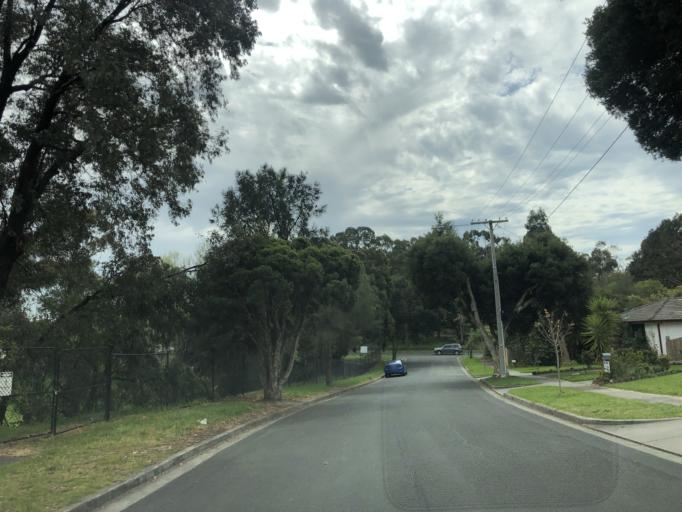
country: AU
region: Victoria
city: Burwood East
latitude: -37.8478
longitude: 145.1416
